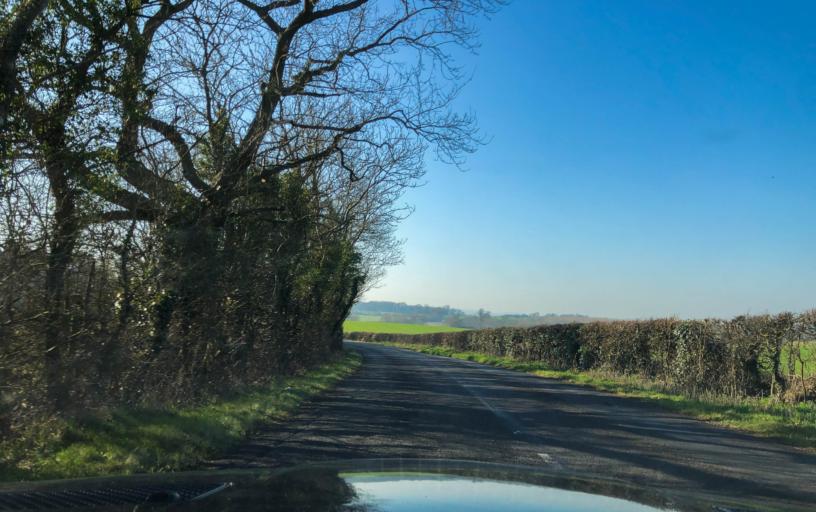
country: GB
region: England
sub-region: Warwickshire
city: Wellesbourne Mountford
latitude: 52.2225
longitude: -1.5664
